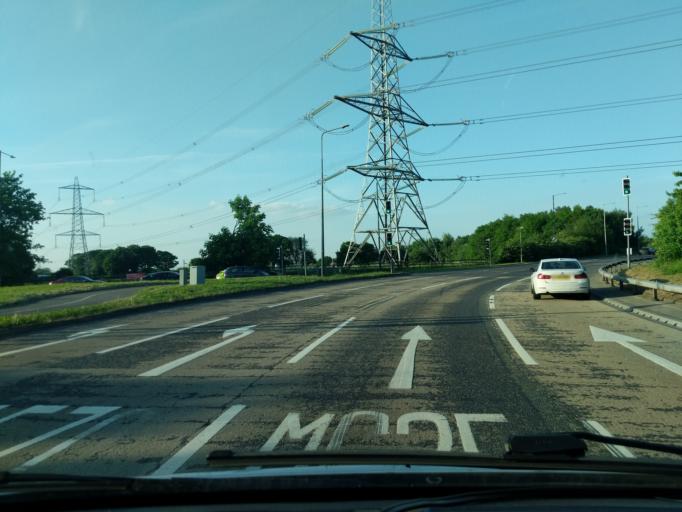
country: GB
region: England
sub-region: Borough of Halton
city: Widnes
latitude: 53.4038
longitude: -2.7475
